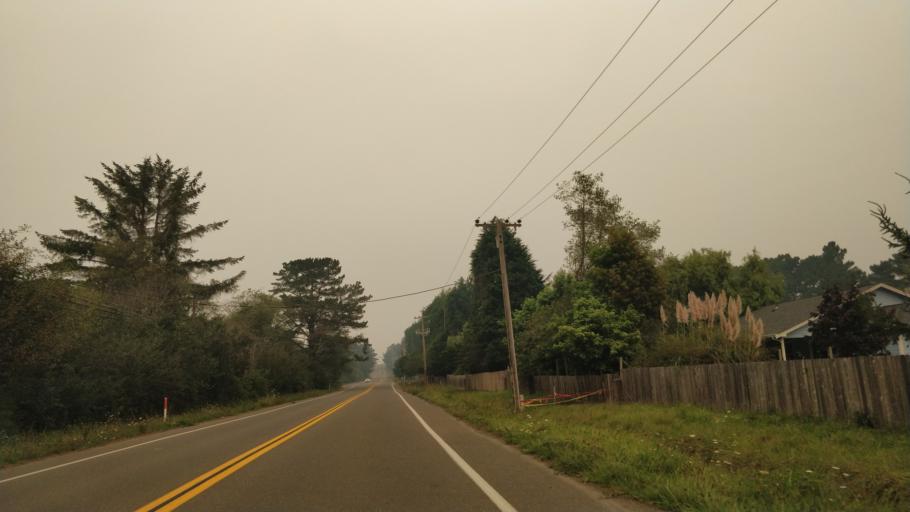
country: US
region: California
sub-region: Humboldt County
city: McKinleyville
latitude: 40.9585
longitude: -124.1008
